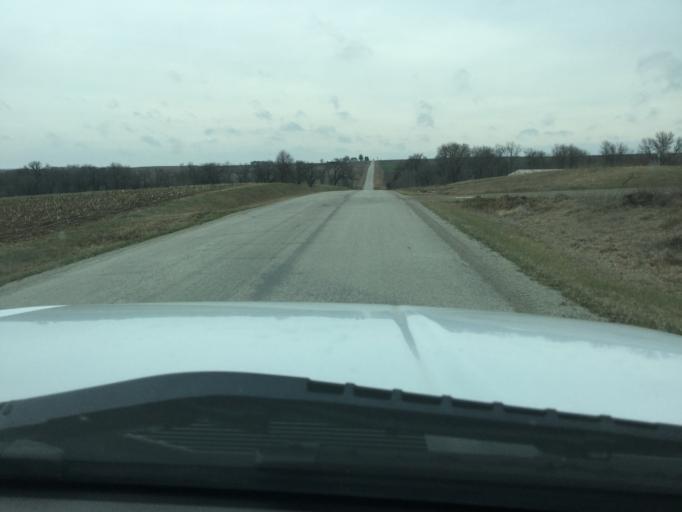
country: US
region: Kansas
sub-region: Nemaha County
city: Sabetha
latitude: 39.8513
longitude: -95.7142
